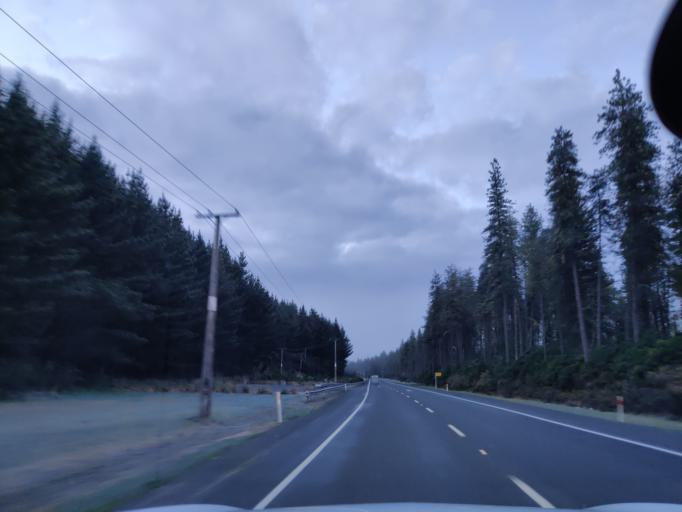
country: NZ
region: Waikato
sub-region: South Waikato District
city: Tokoroa
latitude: -38.3774
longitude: 176.0012
